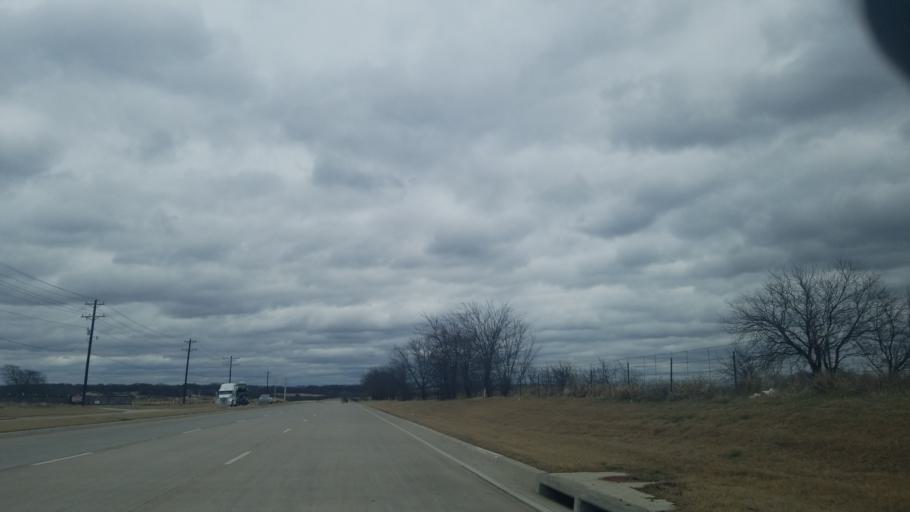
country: US
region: Texas
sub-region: Denton County
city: Trophy Club
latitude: 33.0520
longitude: -97.1929
